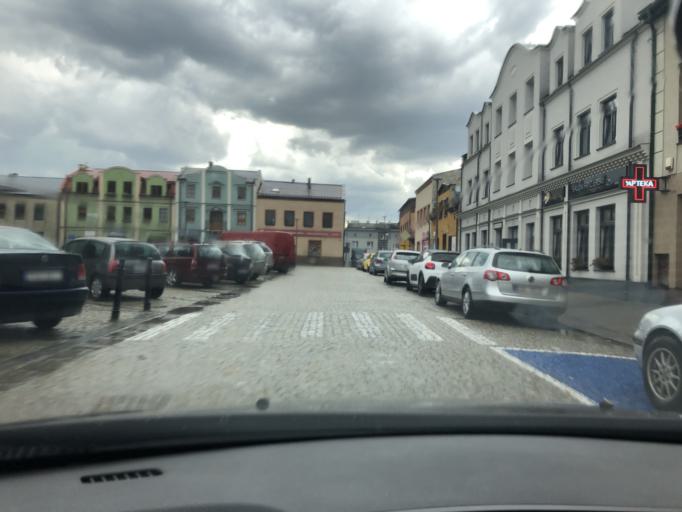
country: PL
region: Lodz Voivodeship
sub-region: Powiat wieruszowski
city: Wieruszow
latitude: 51.2954
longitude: 18.1505
